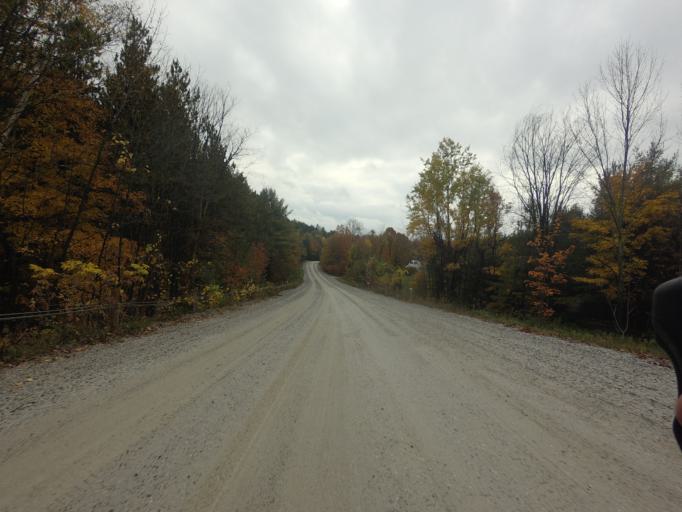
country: CA
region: Ontario
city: Renfrew
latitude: 45.1393
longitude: -76.6678
